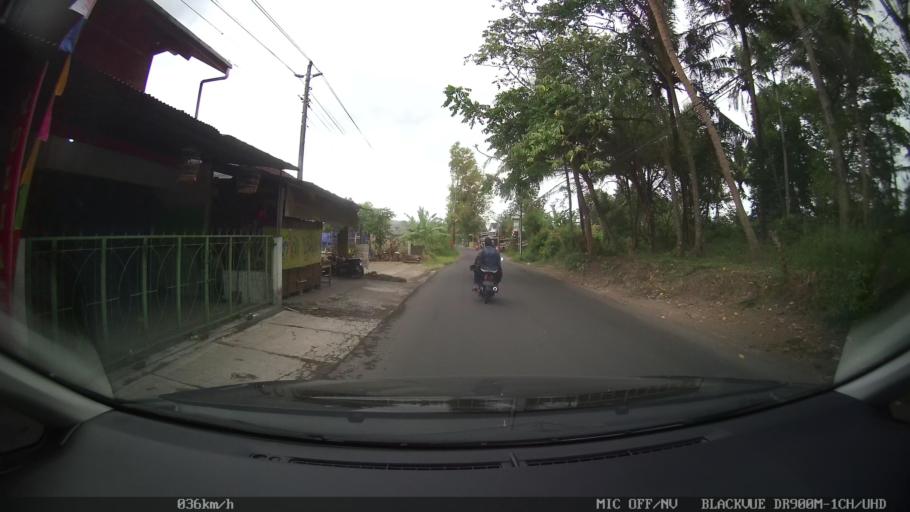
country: ID
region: Daerah Istimewa Yogyakarta
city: Sewon
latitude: -7.8713
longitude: 110.4074
